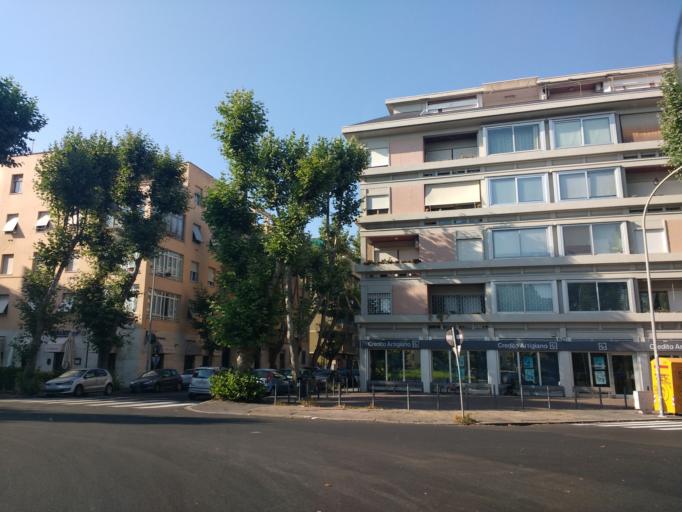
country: IT
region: Latium
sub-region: Citta metropolitana di Roma Capitale
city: Lido di Ostia
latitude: 41.7262
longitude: 12.2910
